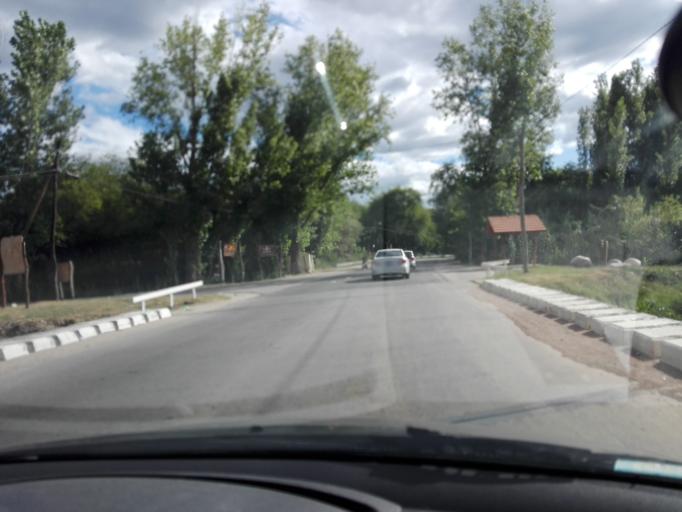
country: AR
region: Cordoba
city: Villa Las Rosas
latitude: -31.9370
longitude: -65.0419
